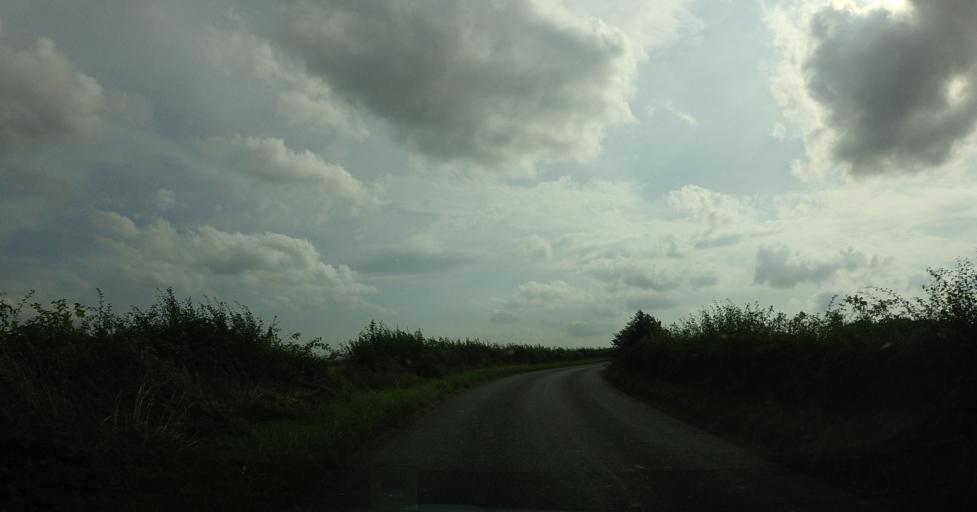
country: GB
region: Scotland
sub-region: Perth and Kinross
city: Auchterarder
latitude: 56.3673
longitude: -3.6944
